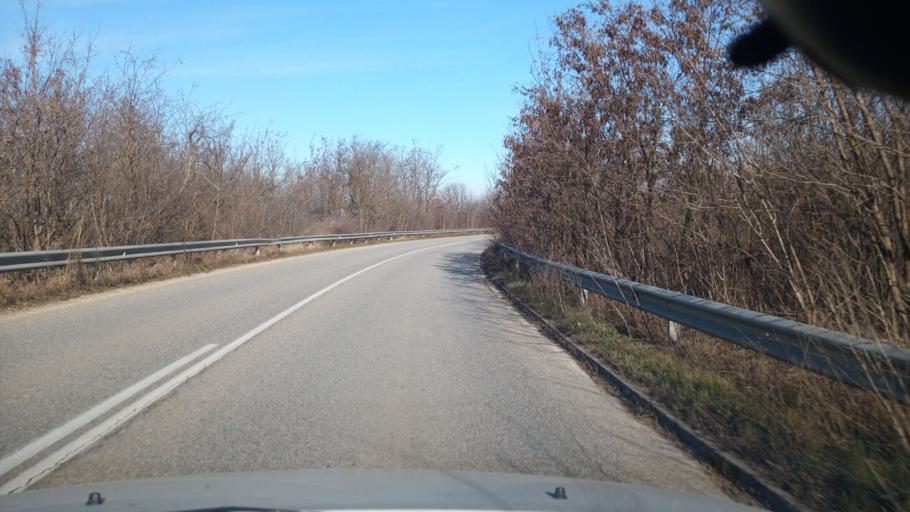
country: BG
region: Pleven
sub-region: Obshtina Pleven
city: Pleven
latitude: 43.4463
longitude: 24.7226
